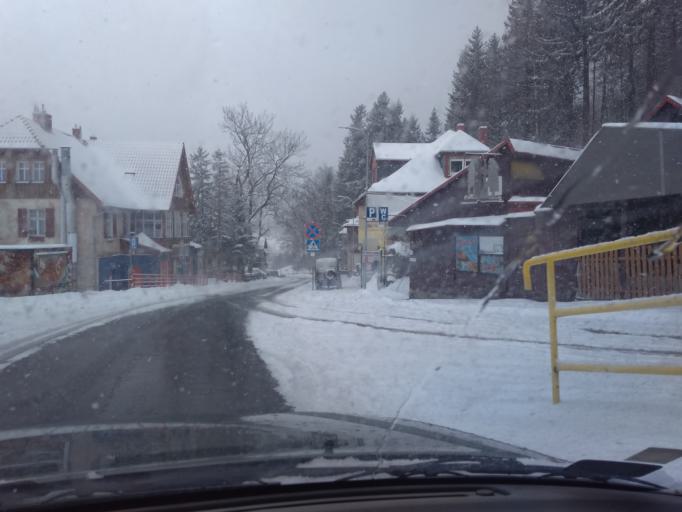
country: PL
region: Lower Silesian Voivodeship
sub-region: Powiat jeleniogorski
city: Karpacz
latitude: 50.7781
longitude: 15.7263
